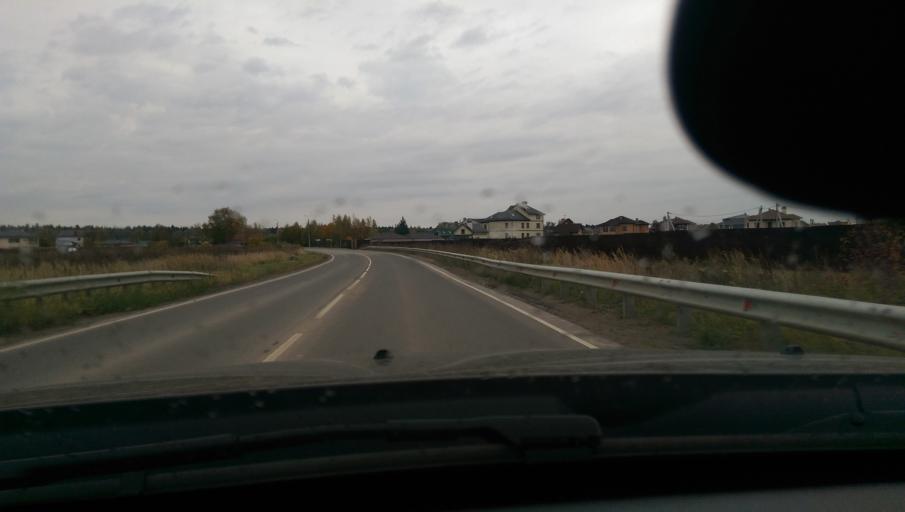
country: RU
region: Moskovskaya
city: Pirogovskiy
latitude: 56.0083
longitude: 37.7221
